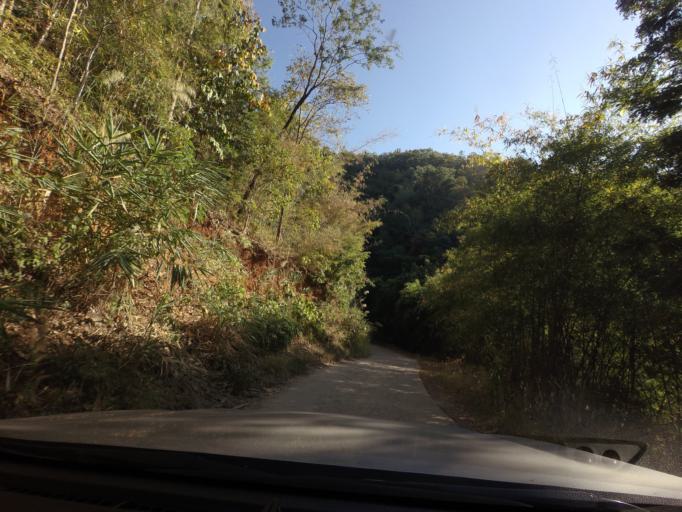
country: TH
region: Lampang
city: Chae Hom
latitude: 18.6081
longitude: 99.6389
